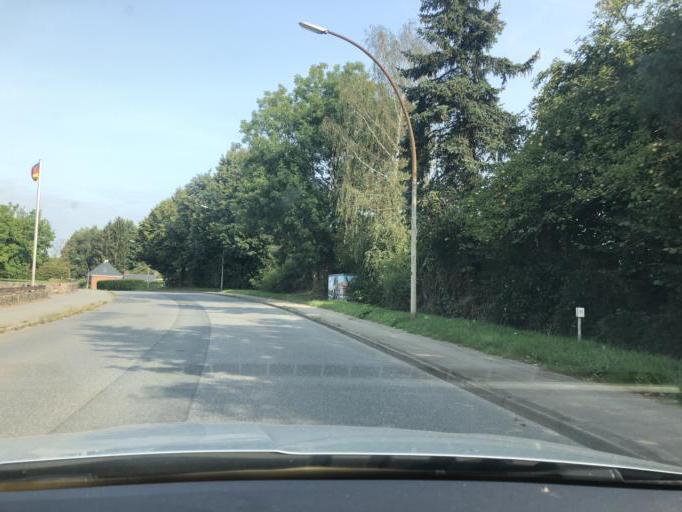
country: DE
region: Schleswig-Holstein
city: Gross Gronau
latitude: 53.8054
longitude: 10.7501
